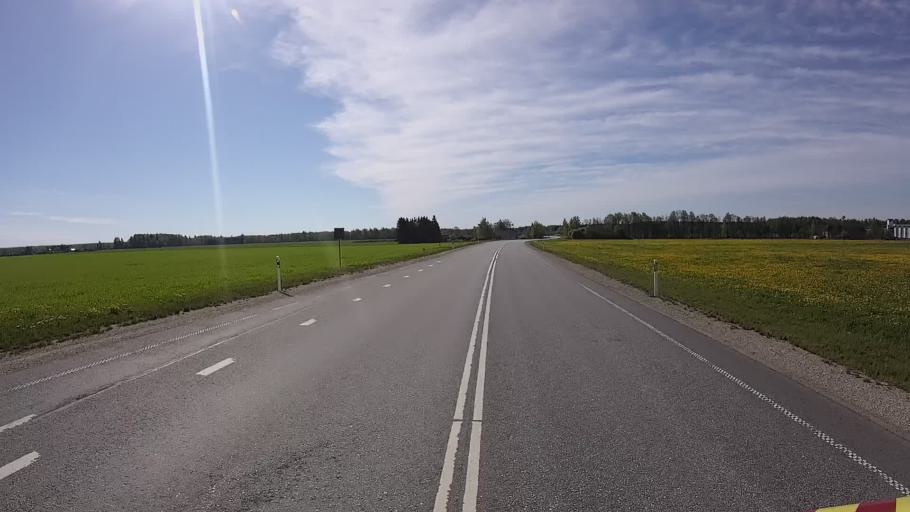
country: EE
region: Tartu
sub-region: Tartu linn
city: Tartu
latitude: 58.3669
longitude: 26.8850
